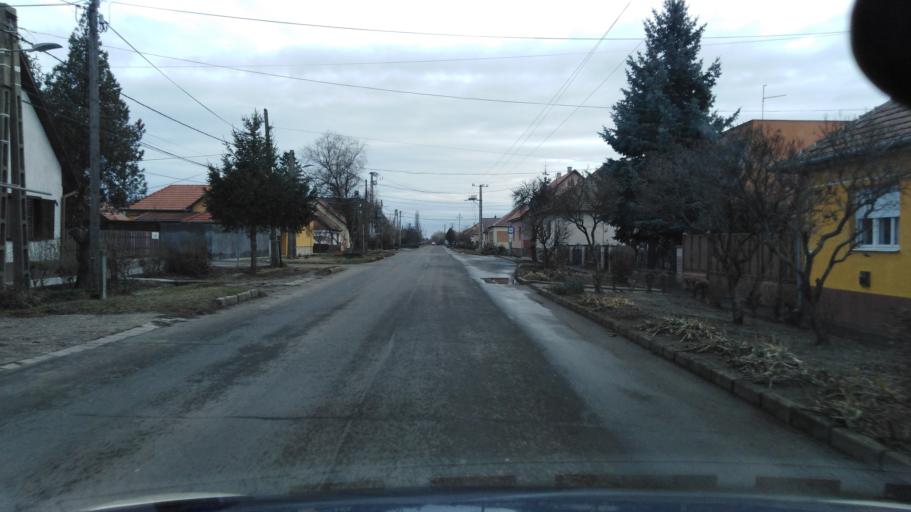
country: HU
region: Heves
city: Hatvan
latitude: 47.6786
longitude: 19.6907
